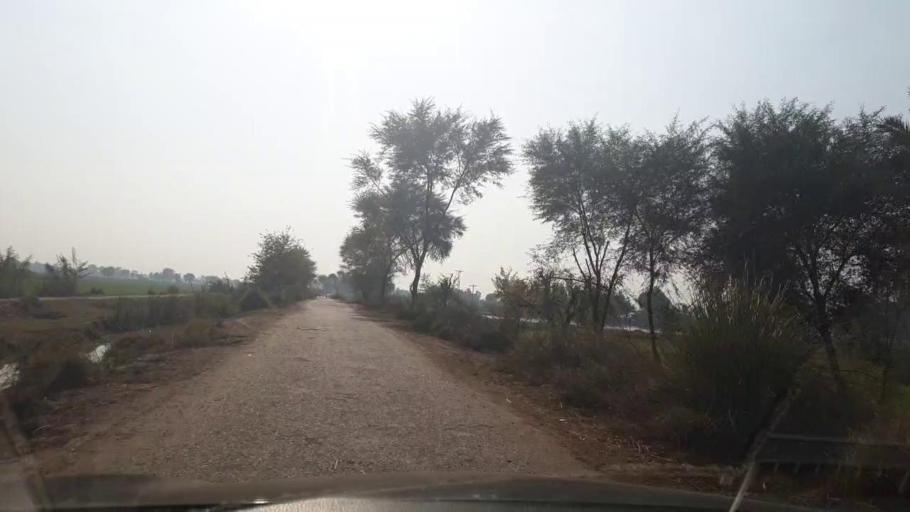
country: PK
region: Sindh
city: Khairpur
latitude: 28.1146
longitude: 69.6398
